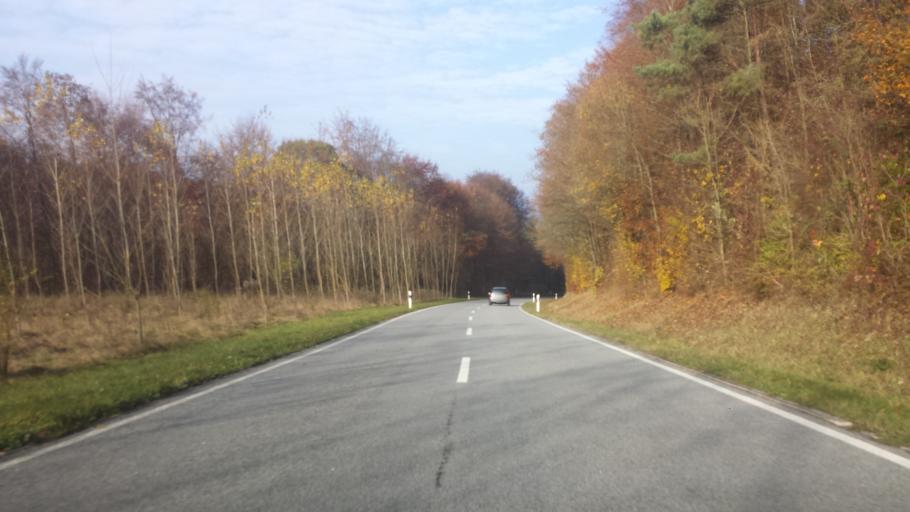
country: DE
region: Baden-Wuerttemberg
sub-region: Karlsruhe Region
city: Obrigheim
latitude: 49.3357
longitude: 9.0657
